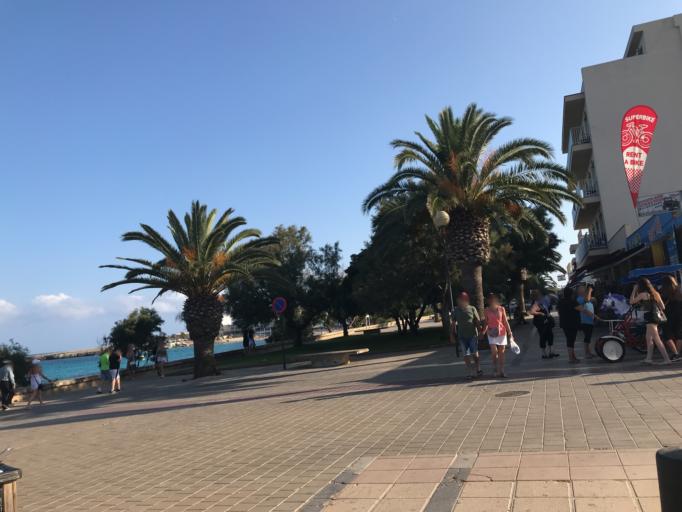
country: ES
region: Balearic Islands
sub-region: Illes Balears
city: Son Servera
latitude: 39.5686
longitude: 3.3738
